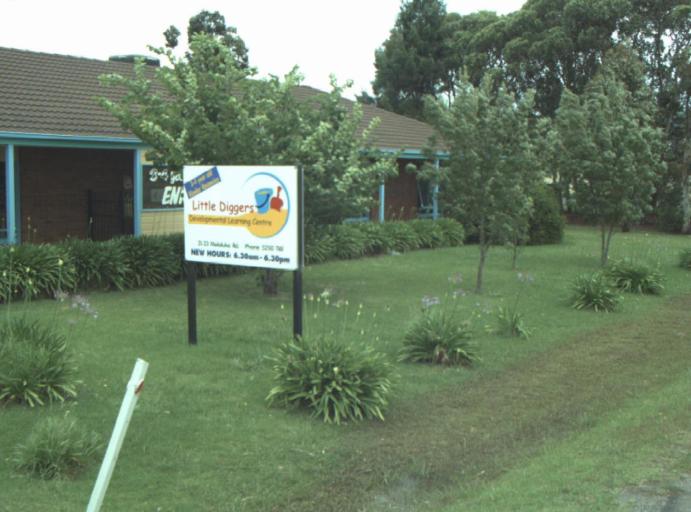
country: AU
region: Victoria
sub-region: Greater Geelong
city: Leopold
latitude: -38.1795
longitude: 144.4570
